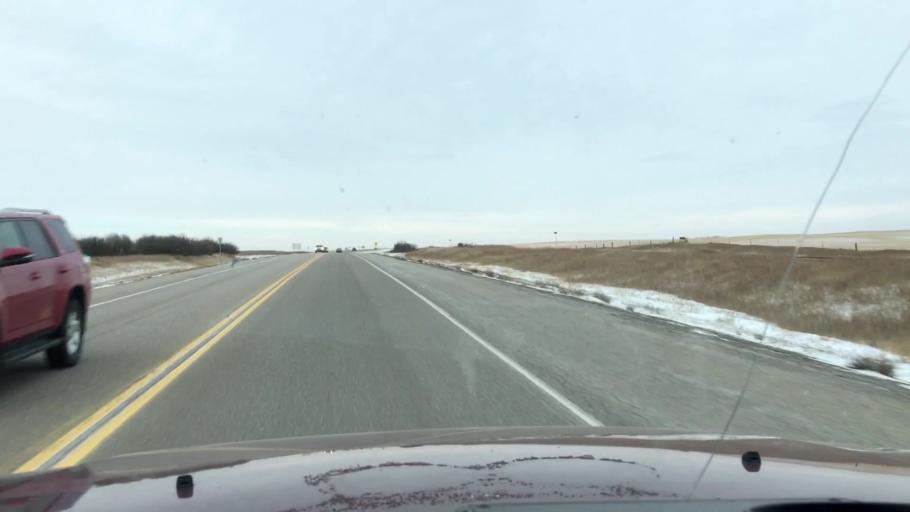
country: CA
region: Saskatchewan
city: Moose Jaw
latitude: 50.8464
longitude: -105.5583
